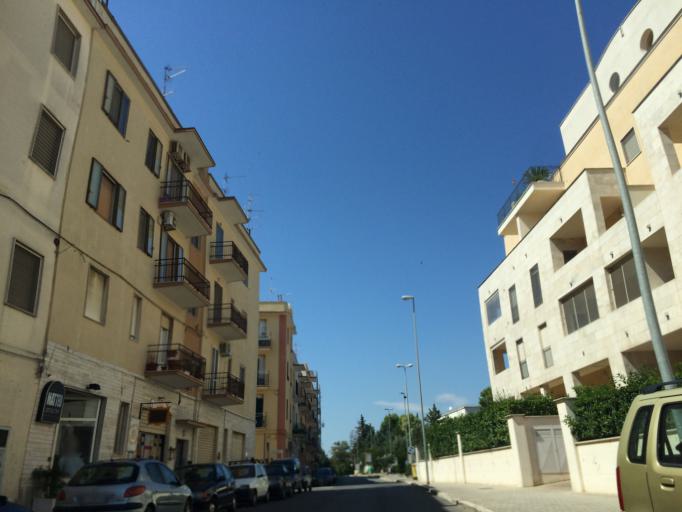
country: IT
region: Basilicate
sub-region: Provincia di Matera
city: Matera
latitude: 40.6732
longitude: 16.6071
